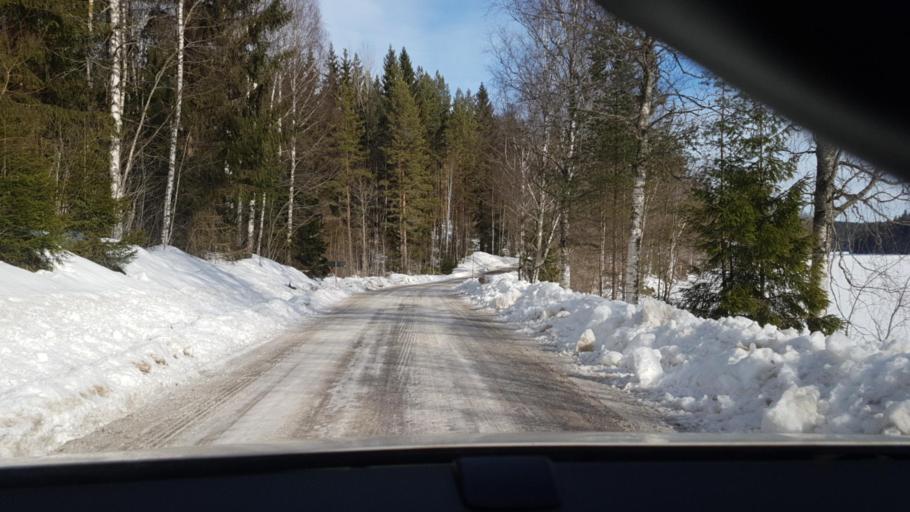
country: NO
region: Hedmark
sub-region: Eidskog
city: Skotterud
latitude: 59.8734
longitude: 11.9769
